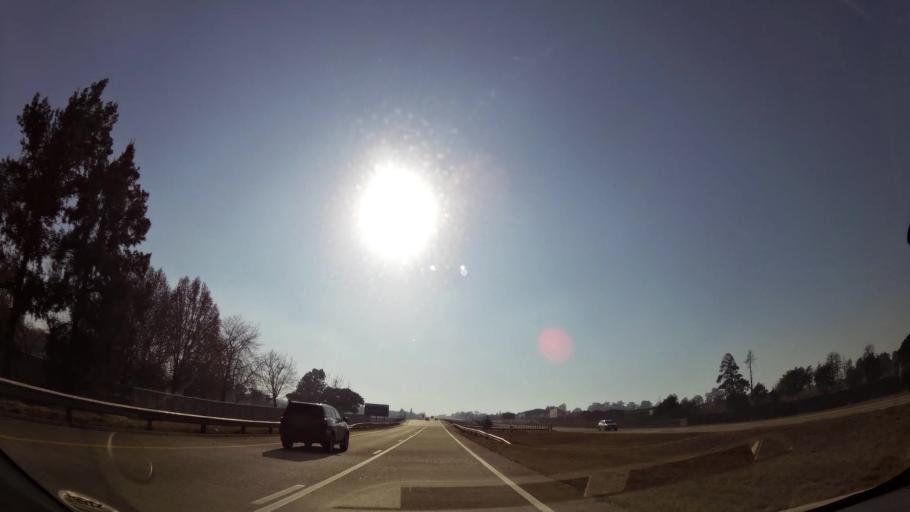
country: ZA
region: Mpumalanga
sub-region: Nkangala District Municipality
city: Witbank
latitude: -25.9178
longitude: 29.2330
